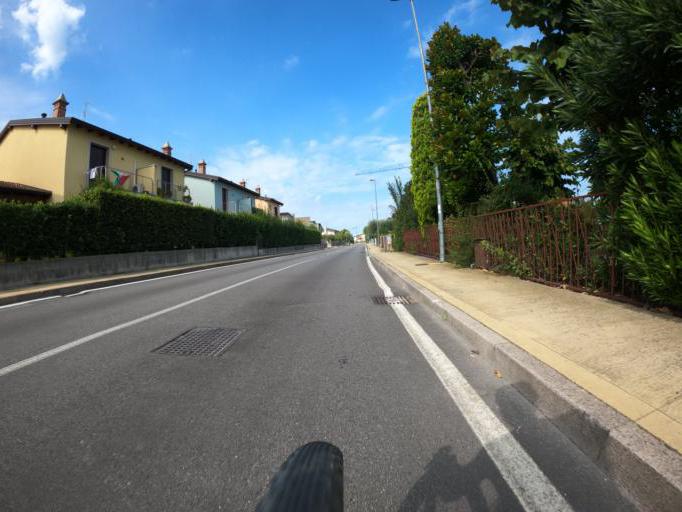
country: IT
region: Veneto
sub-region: Provincia di Verona
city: Peschiera del Garda
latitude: 45.4448
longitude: 10.6645
